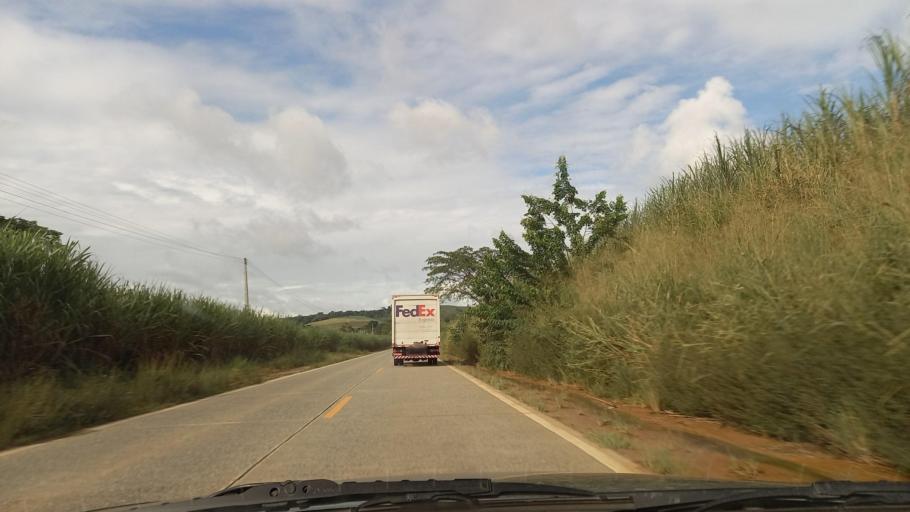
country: BR
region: Pernambuco
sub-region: Catende
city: Catende
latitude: -8.6942
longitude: -35.6856
